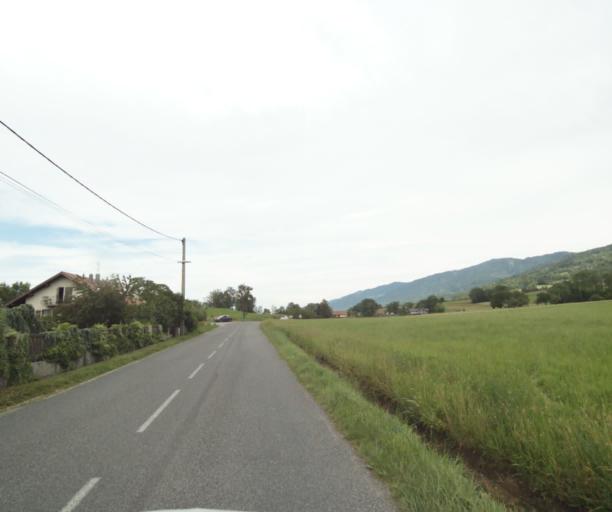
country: FR
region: Rhone-Alpes
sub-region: Departement de la Haute-Savoie
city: Bons-en-Chablais
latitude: 46.2662
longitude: 6.3912
